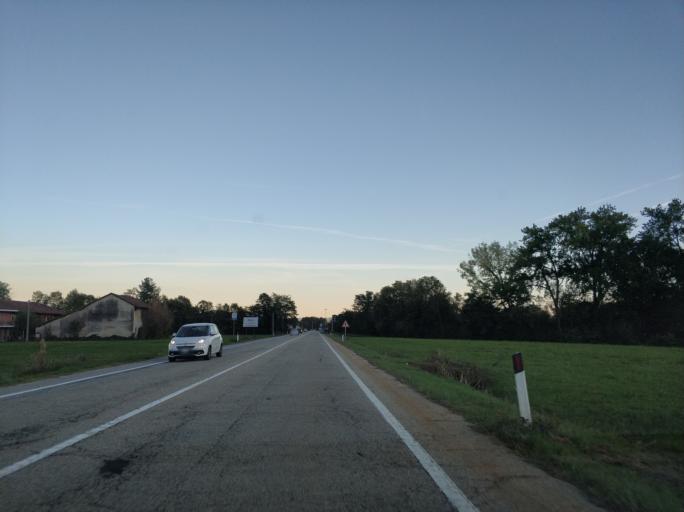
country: IT
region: Piedmont
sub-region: Provincia di Torino
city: Fiano
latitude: 45.2176
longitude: 7.5396
